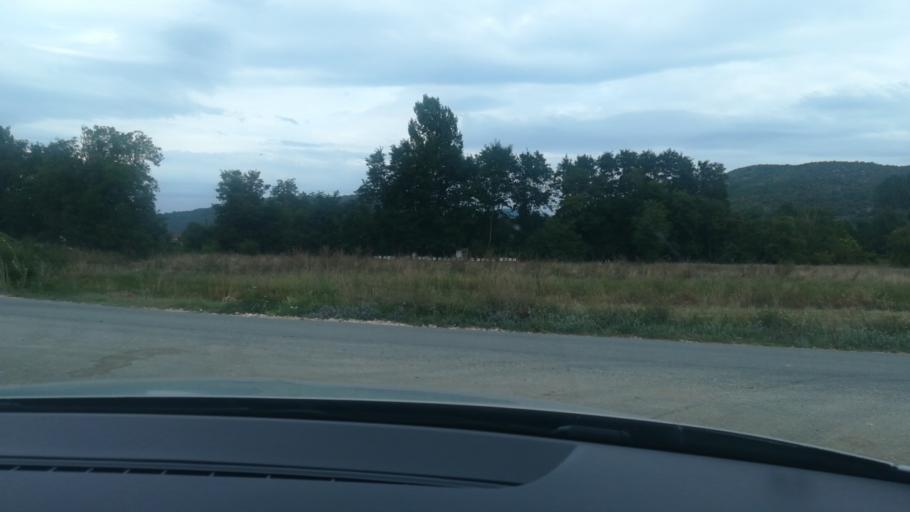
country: MK
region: Debarca
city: Belcista
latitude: 41.2973
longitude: 20.8311
